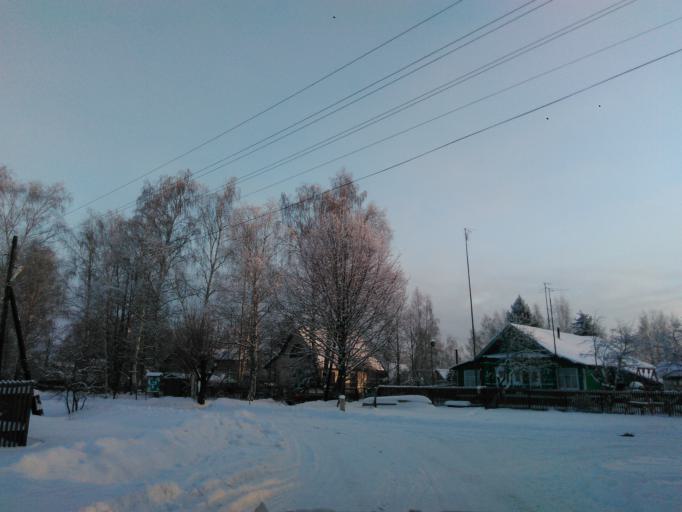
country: RU
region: Tverskaya
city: Zavidovo
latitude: 56.6383
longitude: 36.6278
